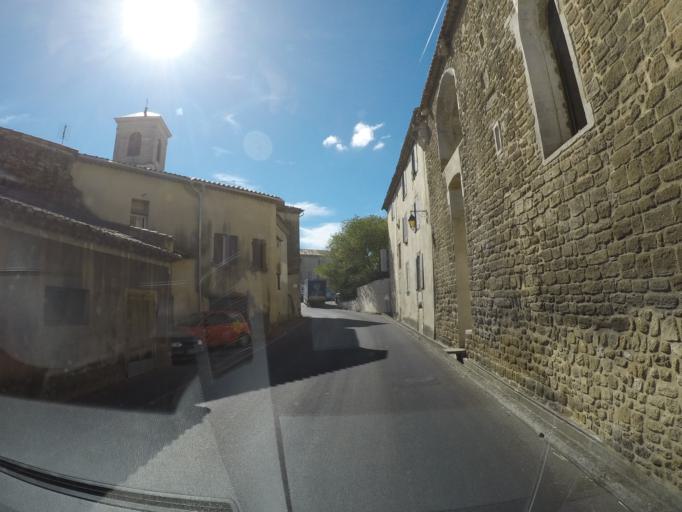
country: FR
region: Rhone-Alpes
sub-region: Departement de la Drome
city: Suze-la-Rousse
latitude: 44.2899
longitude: 4.8398
